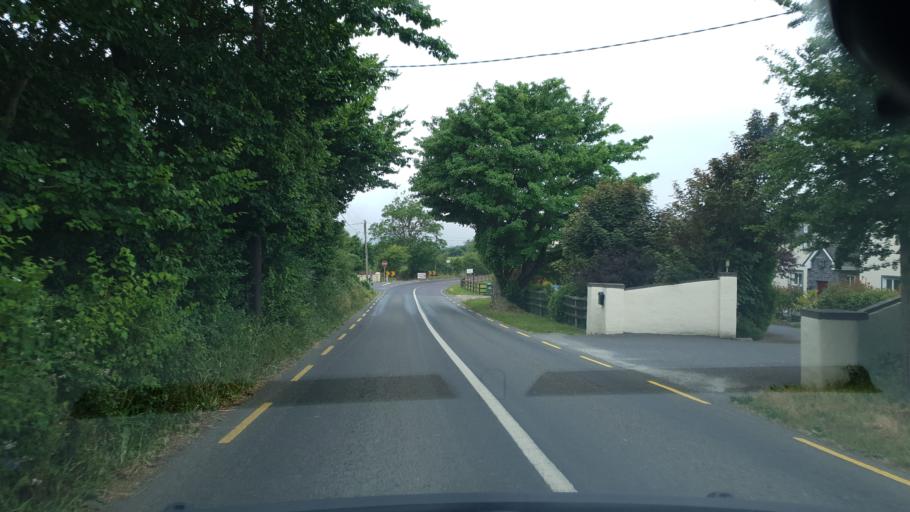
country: IE
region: Munster
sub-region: Ciarrai
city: Tralee
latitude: 52.1592
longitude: -9.6829
